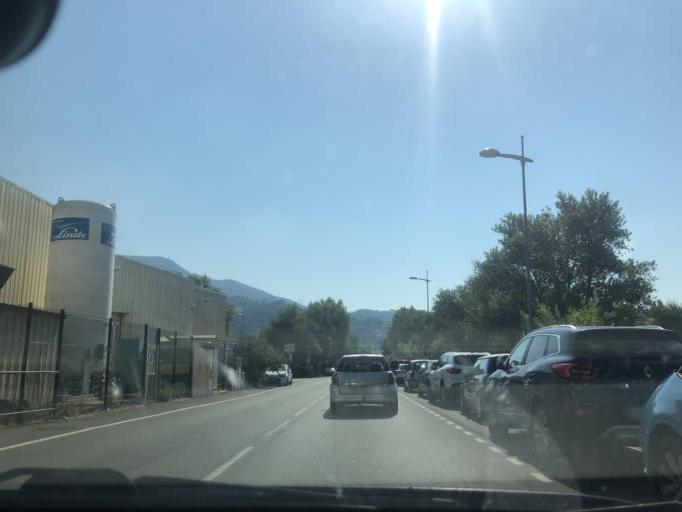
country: FR
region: Provence-Alpes-Cote d'Azur
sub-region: Departement des Alpes-Maritimes
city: Castagniers
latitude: 43.7874
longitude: 7.2089
